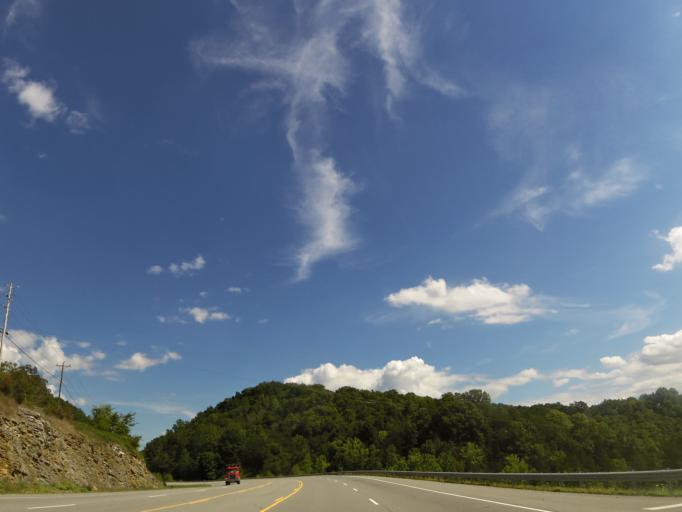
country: US
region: Tennessee
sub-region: Claiborne County
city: Tazewell
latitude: 36.4209
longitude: -83.5185
